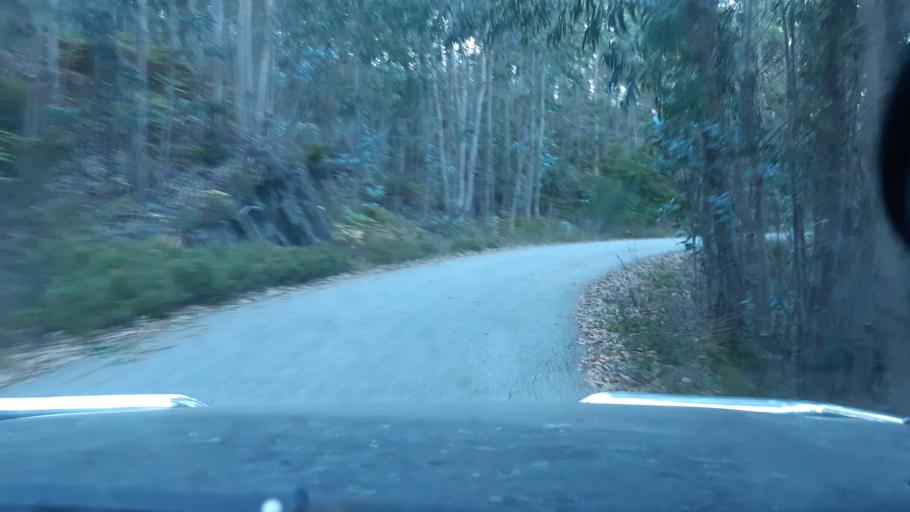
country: PT
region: Aveiro
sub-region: Agueda
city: Aguada de Cima
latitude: 40.5451
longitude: -8.2802
